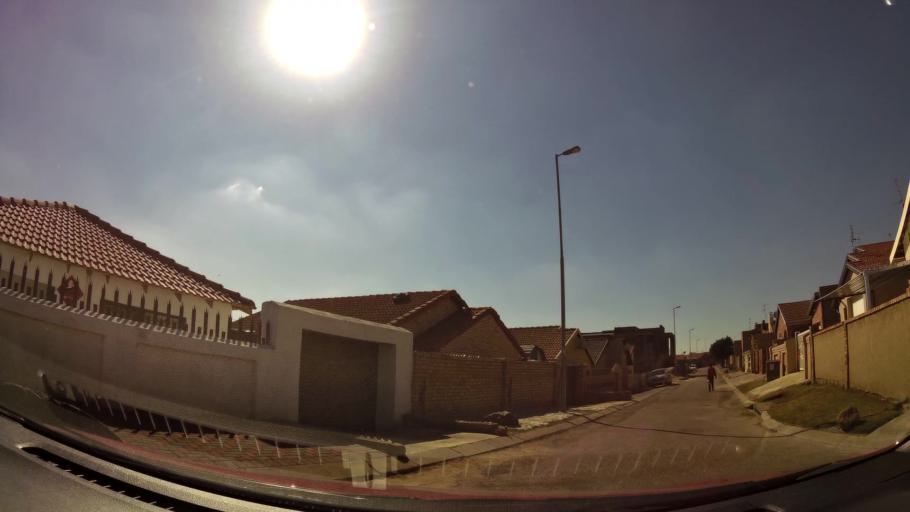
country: ZA
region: Gauteng
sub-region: City of Johannesburg Metropolitan Municipality
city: Soweto
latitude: -26.2328
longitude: 27.8227
